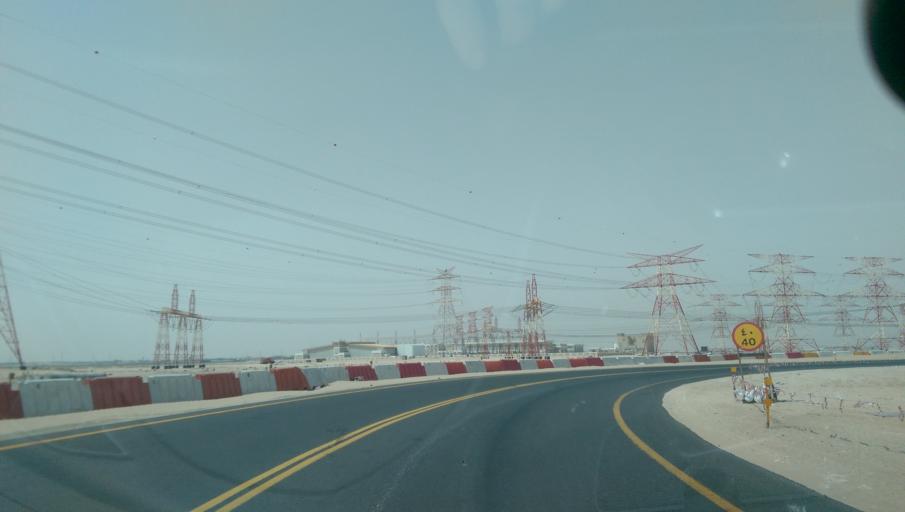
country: AE
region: Abu Dhabi
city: Abu Dhabi
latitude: 24.2959
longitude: 54.5421
